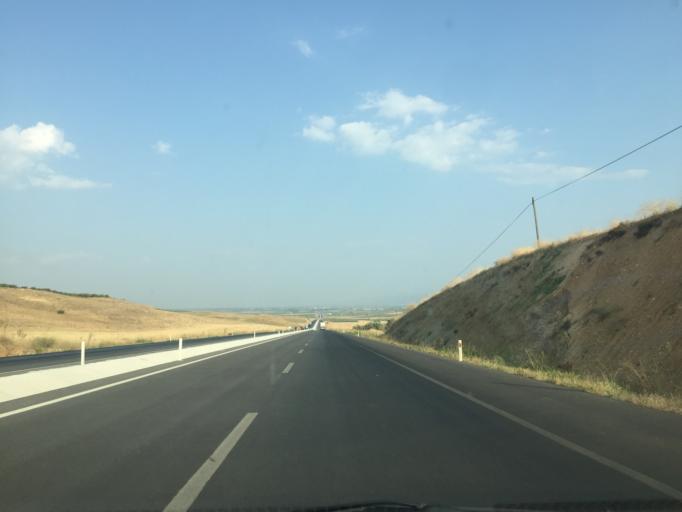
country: TR
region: Manisa
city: Ahmetli
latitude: 38.5758
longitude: 28.0132
